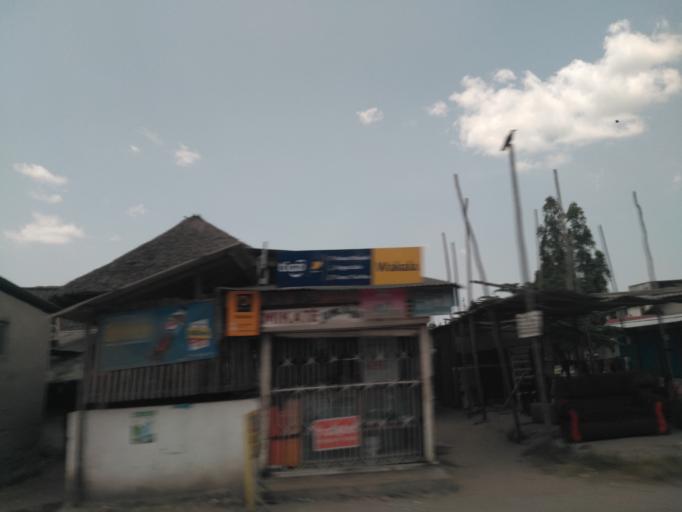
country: TZ
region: Dar es Salaam
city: Dar es Salaam
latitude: -6.8262
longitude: 39.3052
